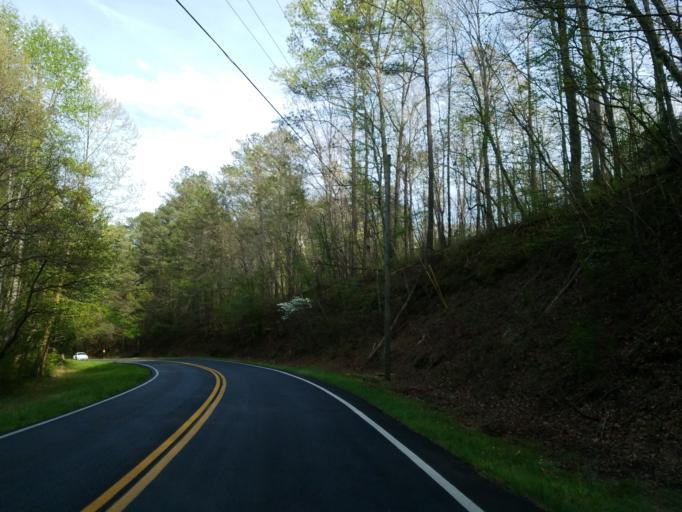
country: US
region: Georgia
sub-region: Pickens County
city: Jasper
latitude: 34.4668
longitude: -84.4044
